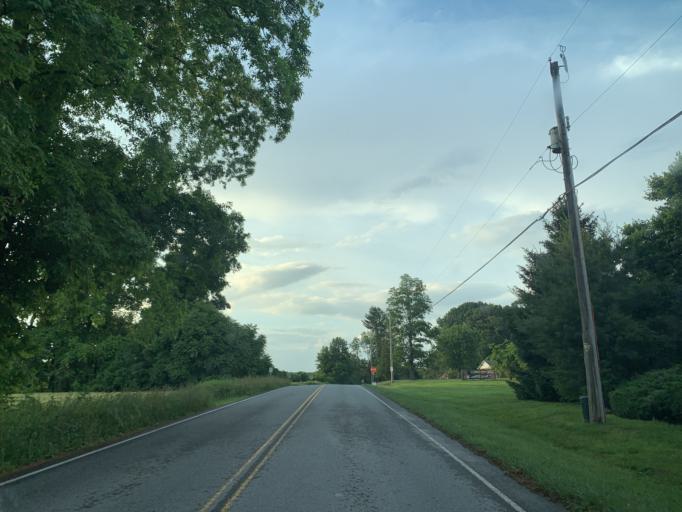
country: US
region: Maryland
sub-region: Cecil County
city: Rising Sun
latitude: 39.7127
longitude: -76.0474
